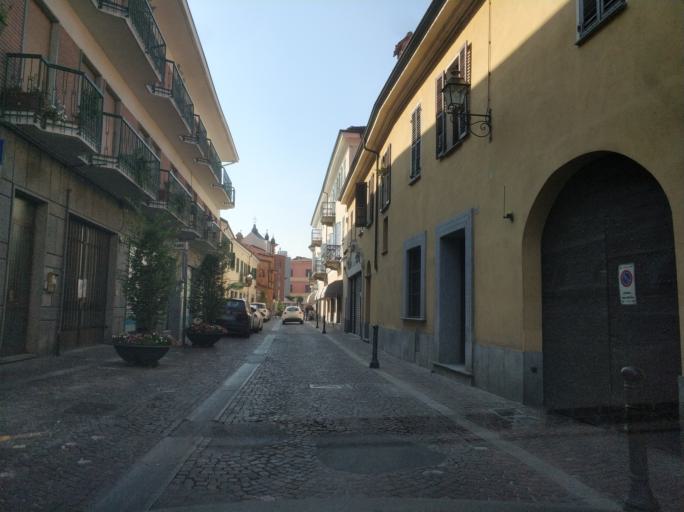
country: IT
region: Piedmont
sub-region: Provincia di Cuneo
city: Bra
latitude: 44.6995
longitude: 7.8495
